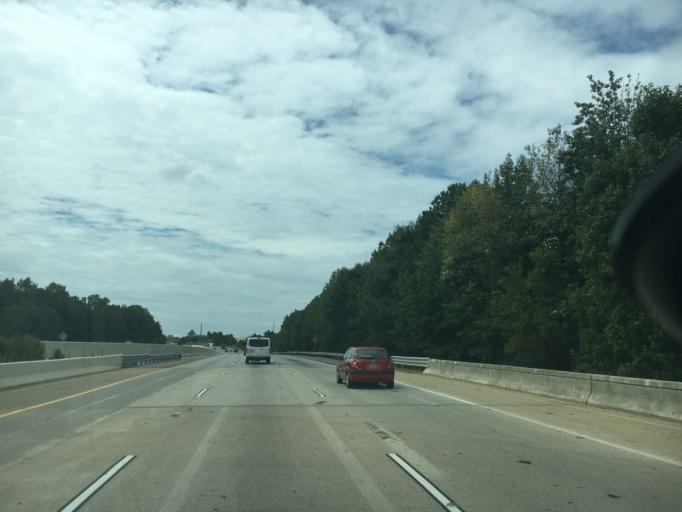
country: US
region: South Carolina
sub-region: Greenville County
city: Mauldin
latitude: 34.7644
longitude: -82.2793
